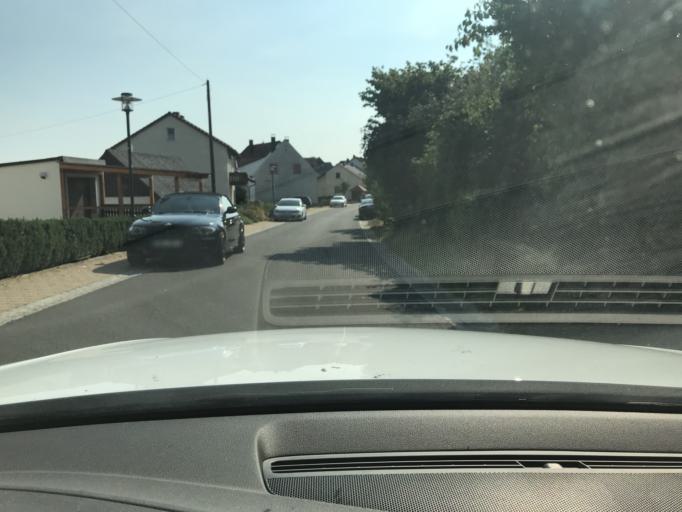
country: DE
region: Bavaria
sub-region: Upper Franconia
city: Pegnitz
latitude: 49.7686
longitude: 11.5986
